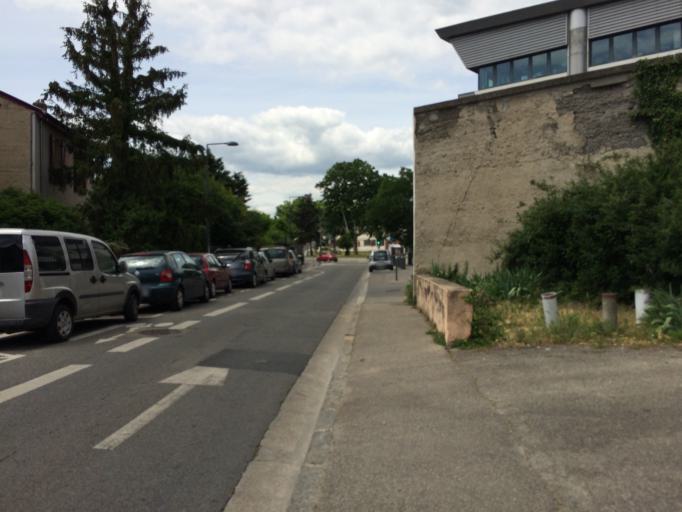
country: FR
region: Rhone-Alpes
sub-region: Departement du Rhone
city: Villeurbanne
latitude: 45.7823
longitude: 4.8798
